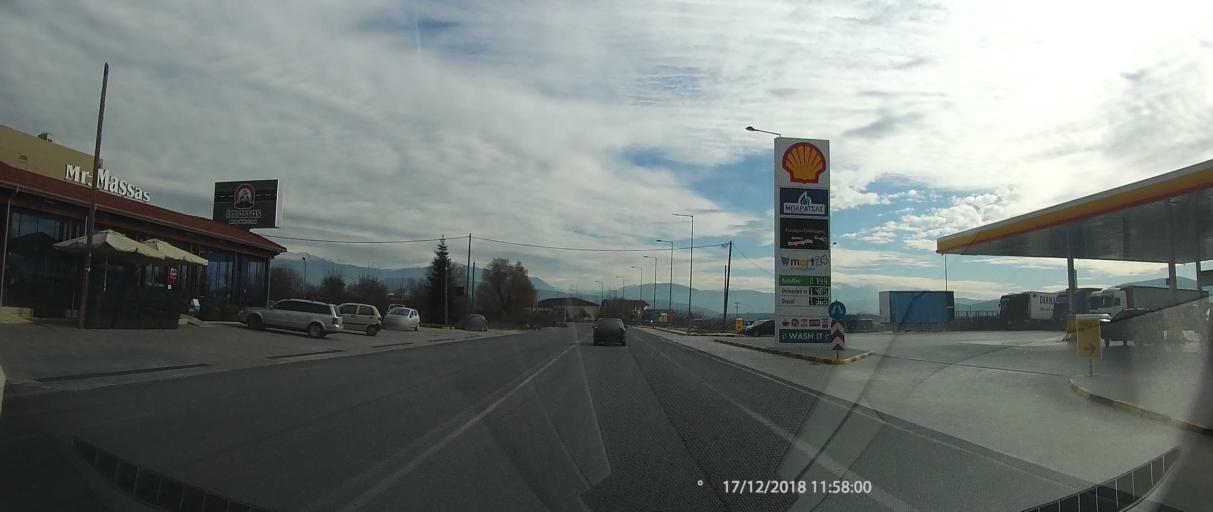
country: GR
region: Epirus
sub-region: Nomos Ioanninon
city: Anatoli
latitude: 39.6224
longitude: 20.8546
